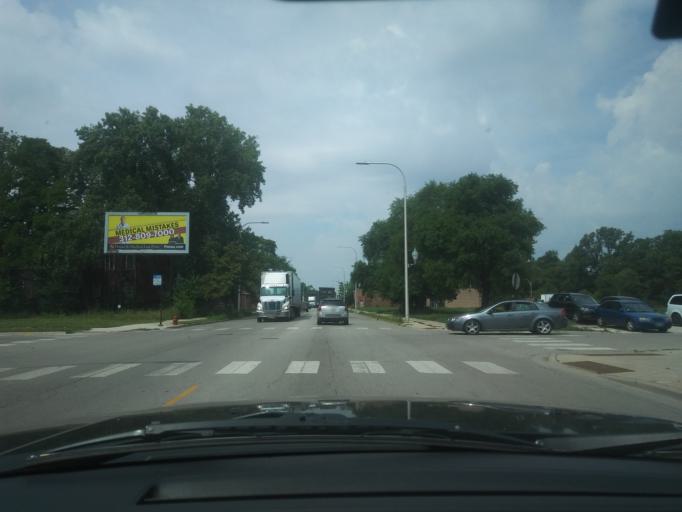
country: US
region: Illinois
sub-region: Cook County
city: Chicago
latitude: 41.7869
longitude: -87.6569
